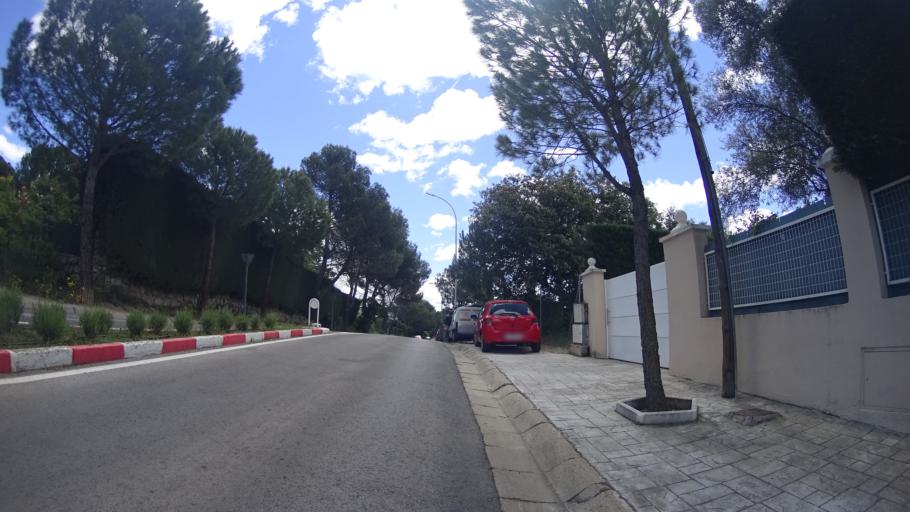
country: ES
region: Madrid
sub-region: Provincia de Madrid
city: Villaviciosa de Odon
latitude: 40.3775
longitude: -3.9370
